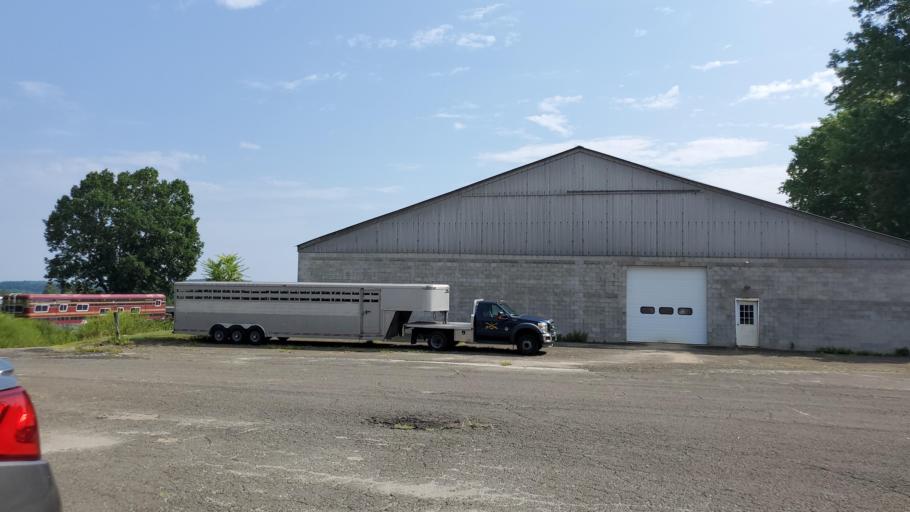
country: US
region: Connecticut
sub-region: Fairfield County
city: Newtown
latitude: 41.4048
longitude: -73.2872
